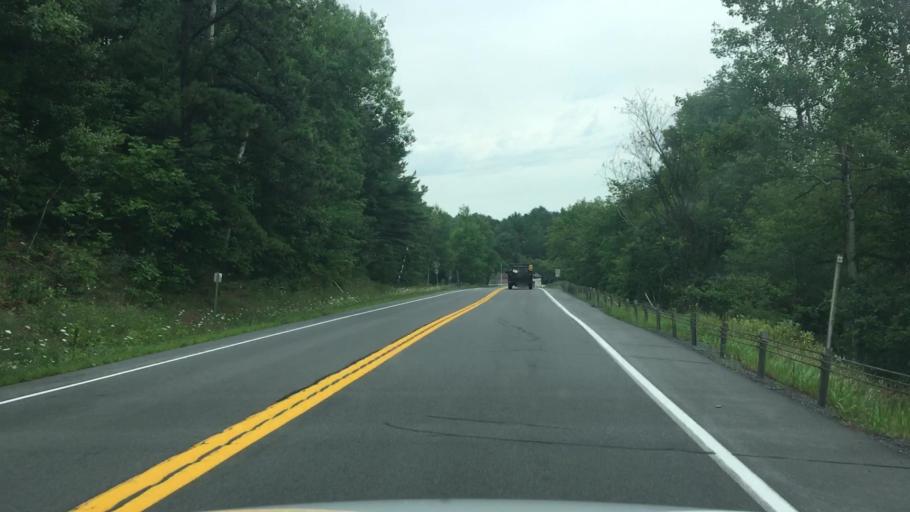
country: US
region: New York
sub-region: Essex County
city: Keeseville
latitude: 44.4586
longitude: -73.6261
